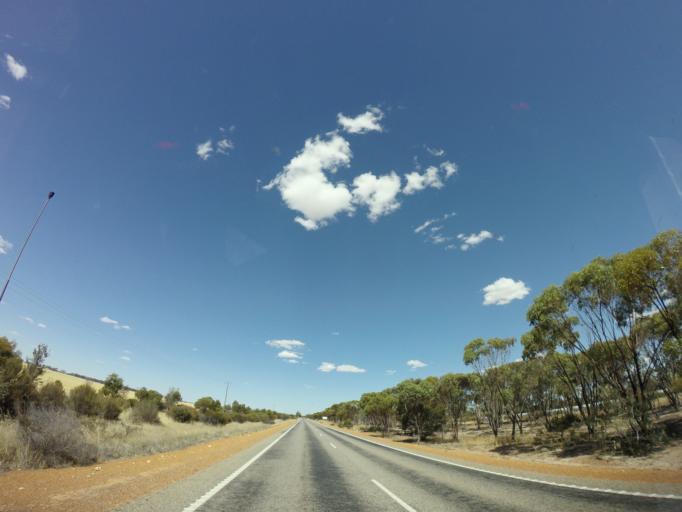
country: AU
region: Western Australia
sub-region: Cunderdin
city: Cunderdin
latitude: -31.6224
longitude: 117.6008
